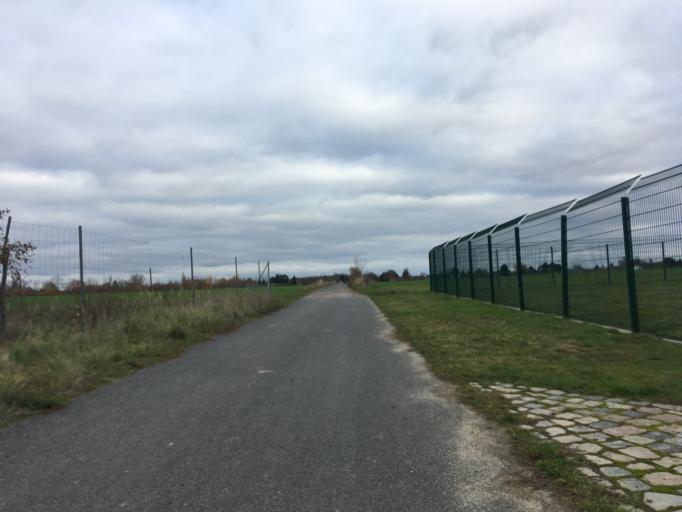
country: DE
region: Berlin
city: Bohnsdorf
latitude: 52.3924
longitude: 13.5528
